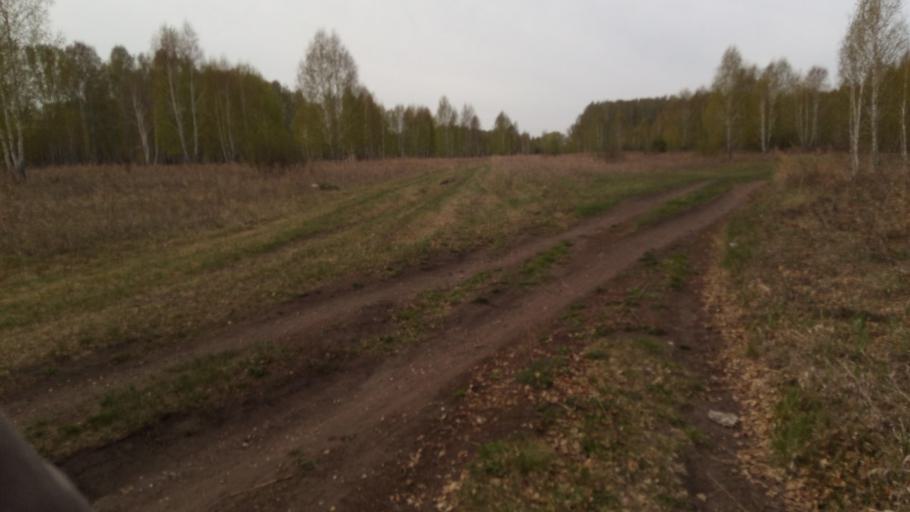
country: RU
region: Chelyabinsk
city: Timiryazevskiy
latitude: 55.0047
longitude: 60.8543
